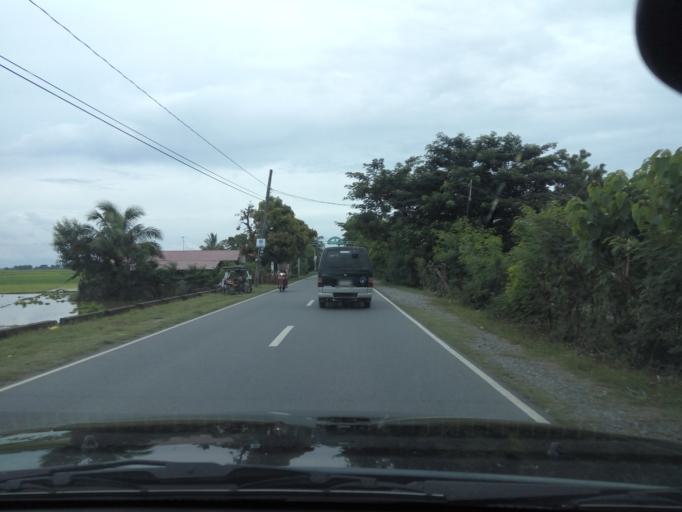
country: PH
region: Central Luzon
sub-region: Province of Nueva Ecija
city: Carmen
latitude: 15.4452
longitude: 120.8342
